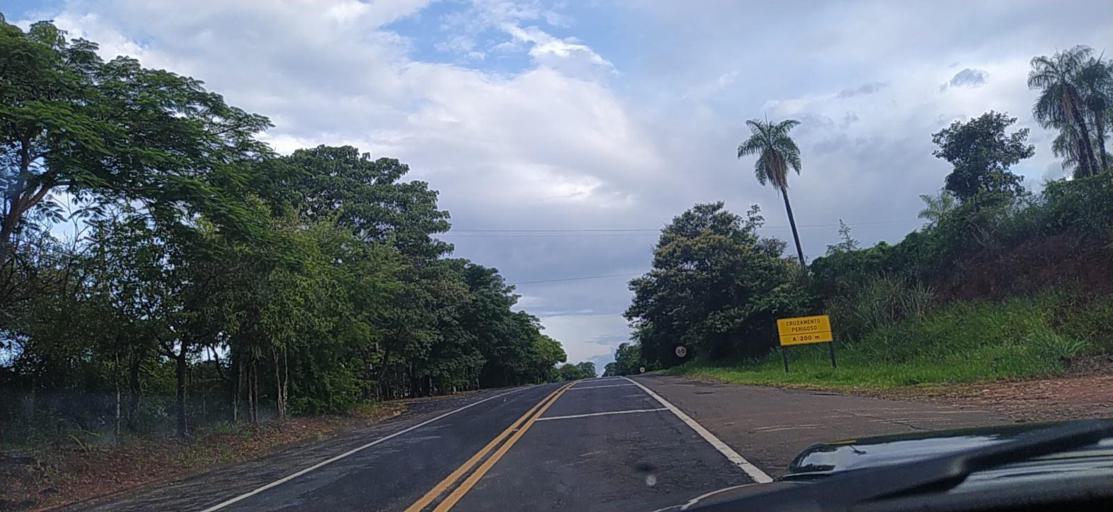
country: BR
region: Sao Paulo
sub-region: Catanduva
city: Catanduva
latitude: -21.1609
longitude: -48.9450
